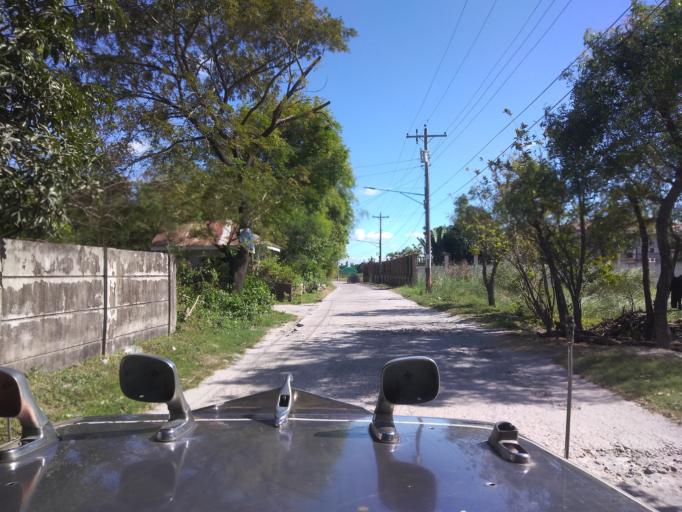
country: PH
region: Central Luzon
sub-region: Province of Pampanga
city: Bacolor
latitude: 15.0108
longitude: 120.6440
